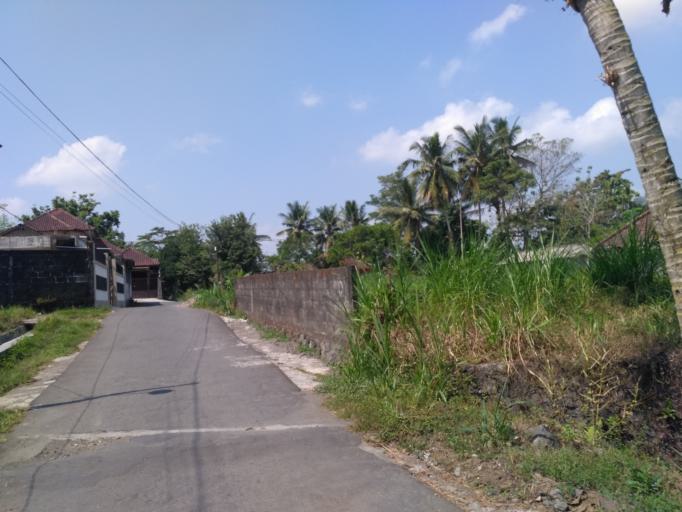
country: ID
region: Daerah Istimewa Yogyakarta
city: Melati
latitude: -7.7050
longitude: 110.4140
